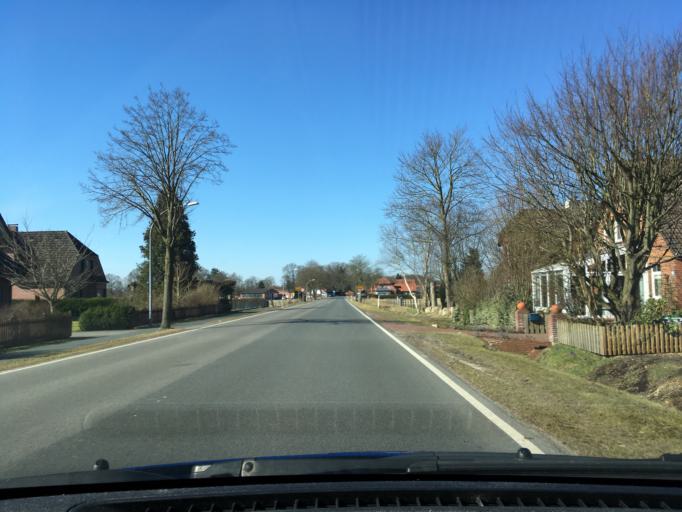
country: DE
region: Lower Saxony
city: Brockel
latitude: 53.0958
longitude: 9.5161
